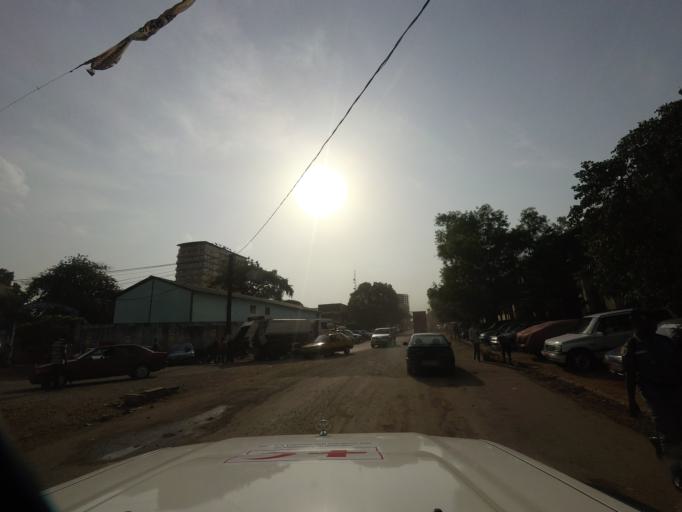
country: GN
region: Conakry
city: Camayenne
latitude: 9.5150
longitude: -13.7137
